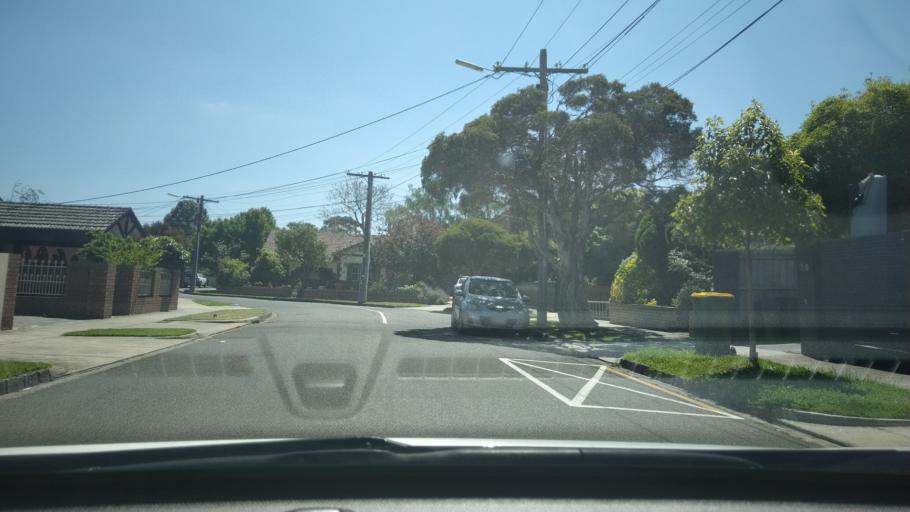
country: AU
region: Victoria
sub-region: Glen Eira
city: Caulfield South
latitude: -37.8920
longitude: 145.0323
